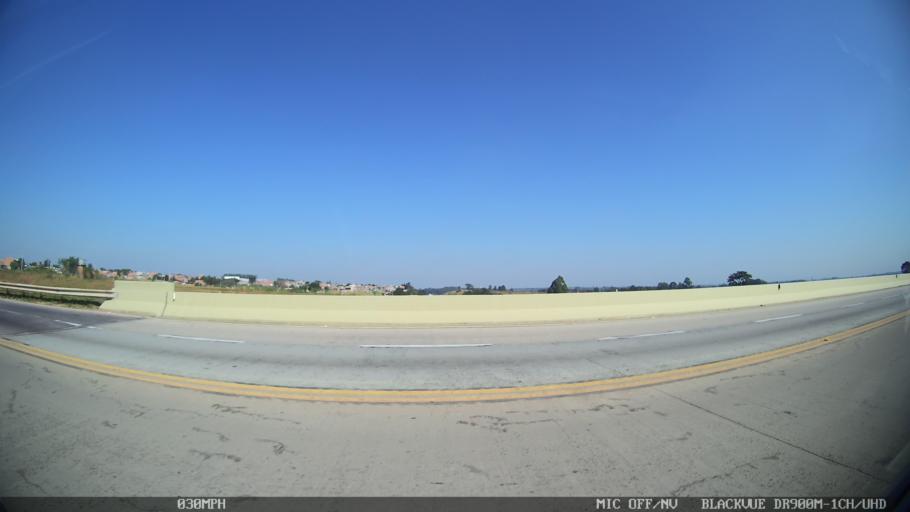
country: BR
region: Sao Paulo
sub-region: Indaiatuba
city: Indaiatuba
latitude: -23.0259
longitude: -47.1232
